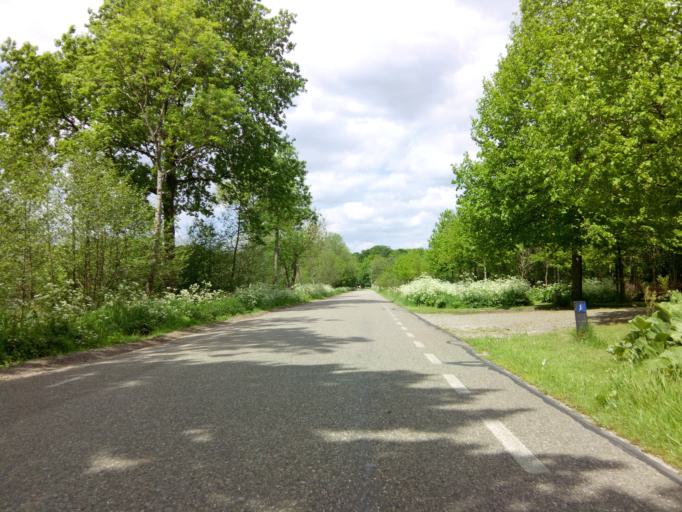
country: NL
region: Gelderland
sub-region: Gemeente Ede
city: Ederveen
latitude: 52.0691
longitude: 5.5542
